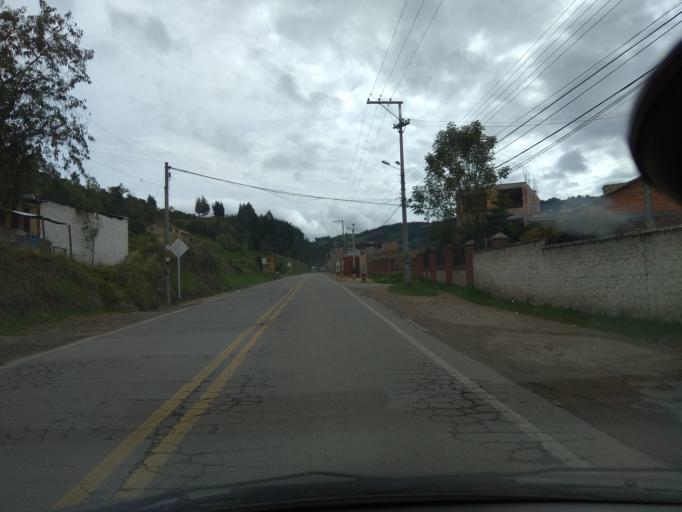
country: CO
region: Boyaca
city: Duitama
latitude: 5.8331
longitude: -73.0231
